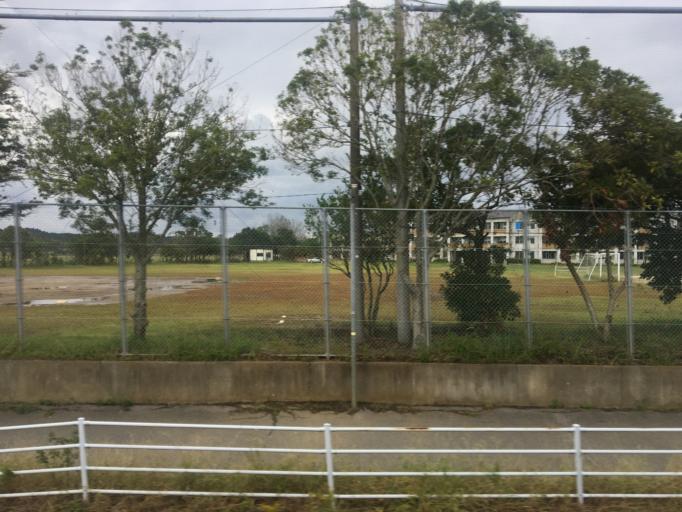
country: JP
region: Chiba
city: Togane
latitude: 35.5499
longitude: 140.3460
